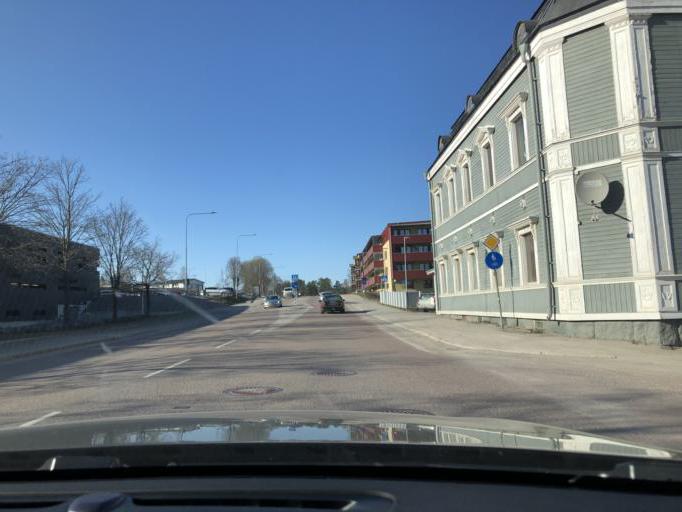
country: SE
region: Gaevleborg
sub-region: Hudiksvalls Kommun
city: Hudiksvall
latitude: 61.7305
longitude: 17.1007
